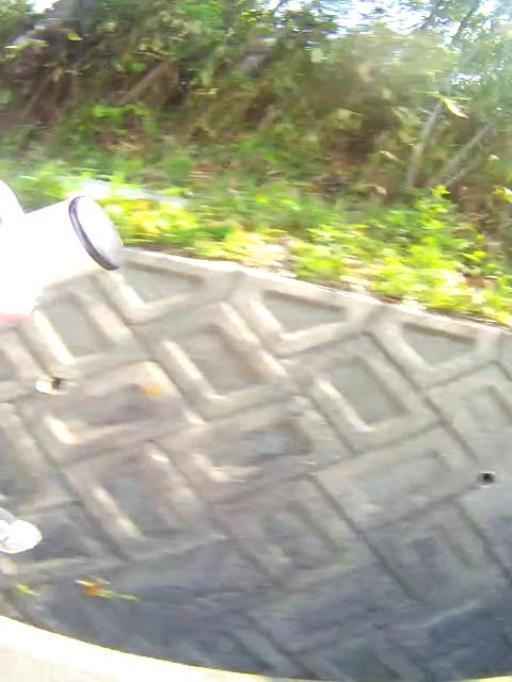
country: JP
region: Osaka
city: Matsubara
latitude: 34.5278
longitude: 135.5678
